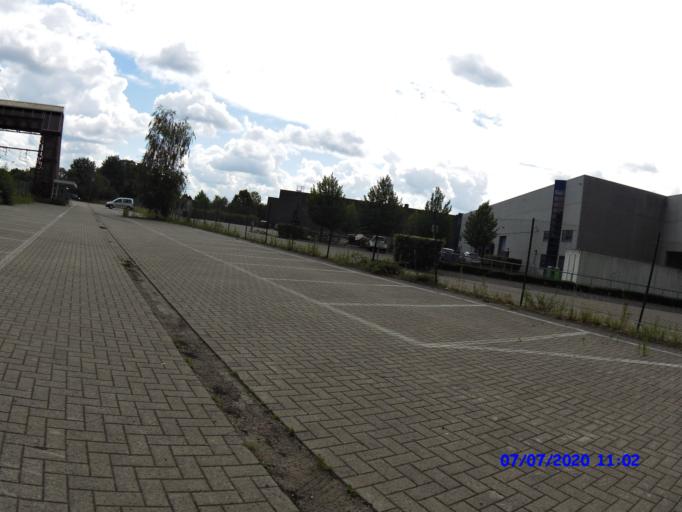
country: BE
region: Flanders
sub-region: Provincie Antwerpen
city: Vorselaar
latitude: 51.1683
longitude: 4.7844
